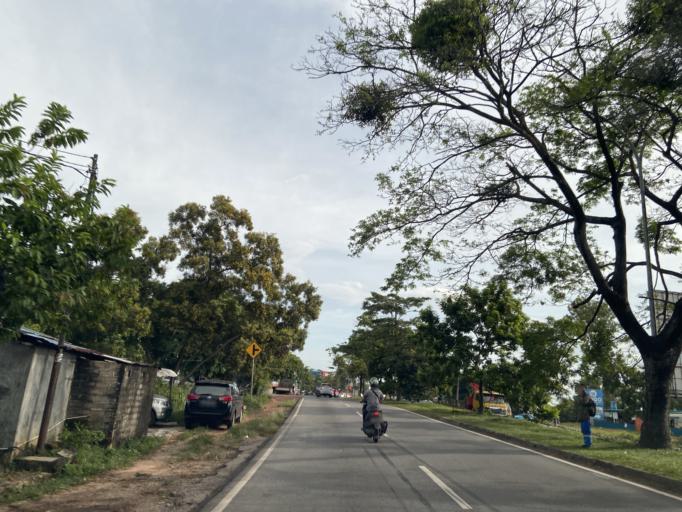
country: SG
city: Singapore
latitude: 1.1491
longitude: 104.0231
